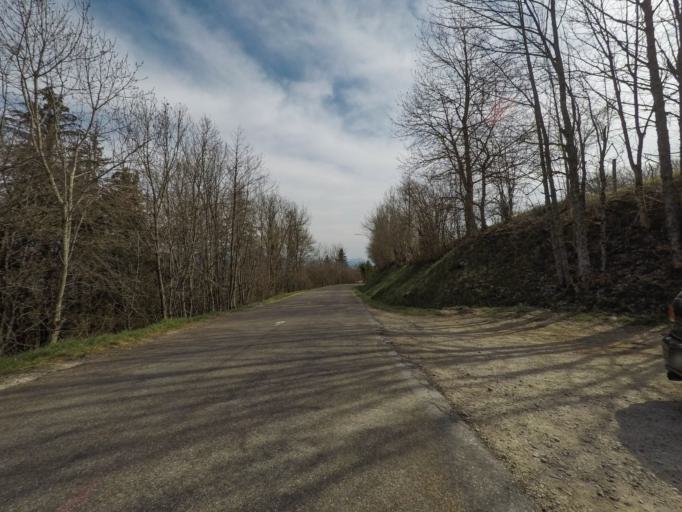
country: FR
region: Rhone-Alpes
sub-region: Departement de la Haute-Savoie
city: Collonges-sous-Saleve
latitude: 46.1281
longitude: 6.1752
